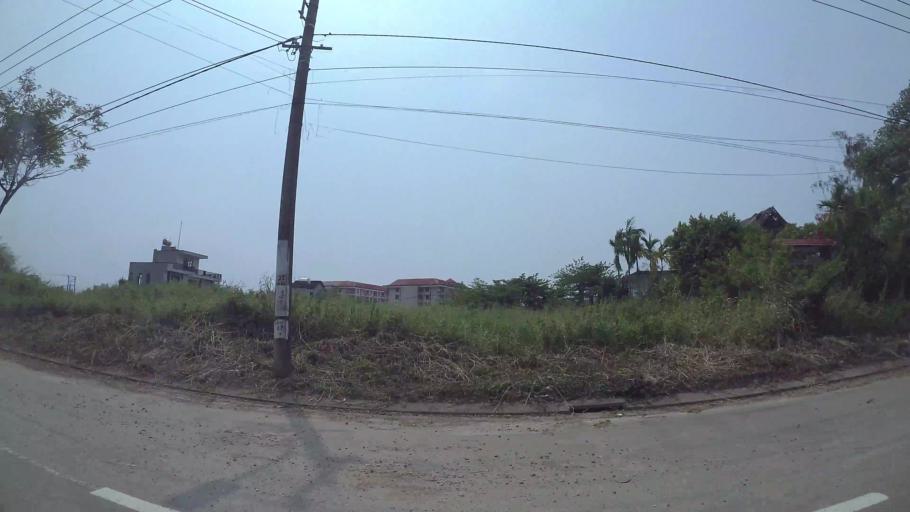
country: VN
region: Da Nang
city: Son Tra
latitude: 16.1072
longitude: 108.2628
